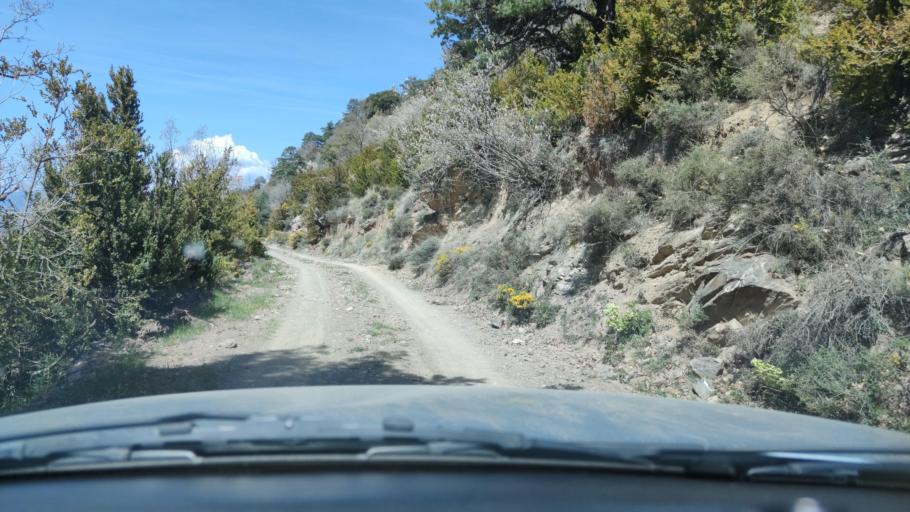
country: ES
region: Catalonia
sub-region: Provincia de Lleida
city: Sort
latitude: 42.3085
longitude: 1.1563
